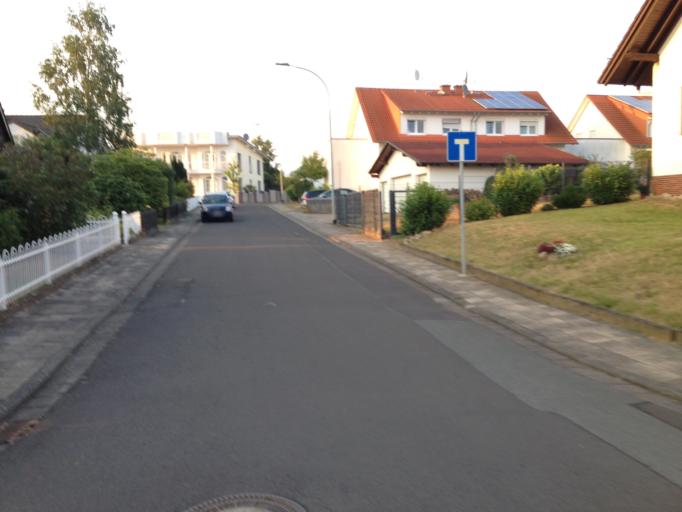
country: DE
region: Hesse
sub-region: Regierungsbezirk Giessen
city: Langgons
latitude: 50.5220
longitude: 8.6556
